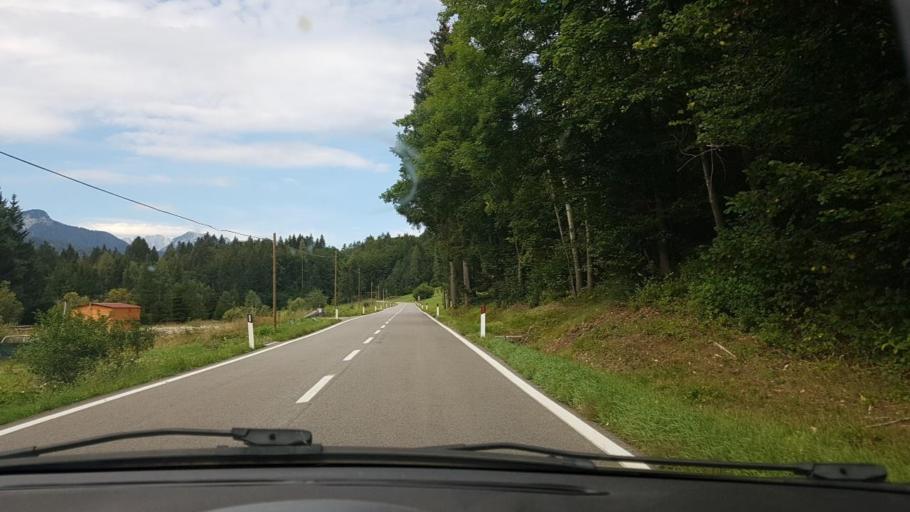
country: AT
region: Carinthia
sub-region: Politischer Bezirk Villach Land
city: Arnoldstein
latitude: 46.4993
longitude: 13.6818
